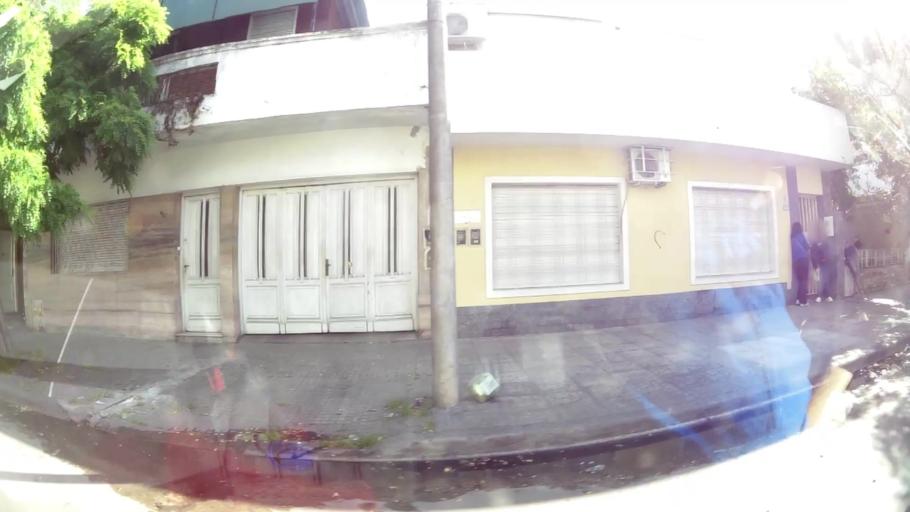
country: AR
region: Buenos Aires
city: San Justo
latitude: -34.6448
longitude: -58.5568
